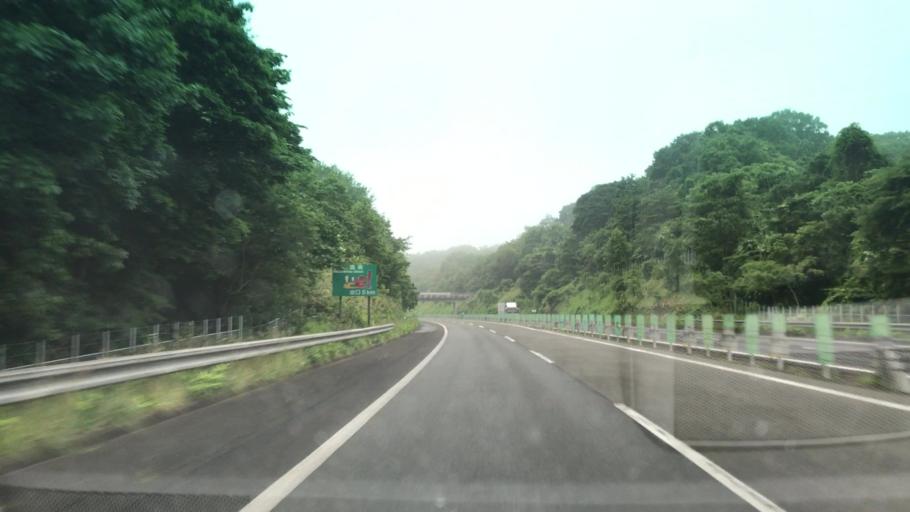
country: JP
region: Hokkaido
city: Shiraoi
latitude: 42.4838
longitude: 141.2248
